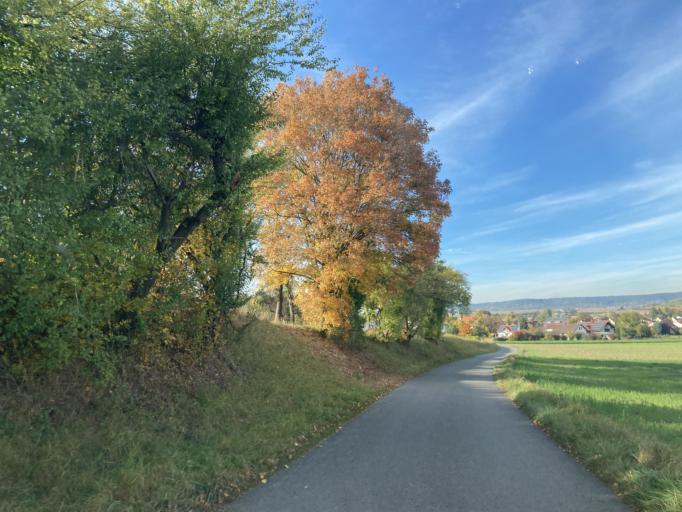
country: DE
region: Baden-Wuerttemberg
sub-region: Tuebingen Region
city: Rottenburg
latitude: 48.5211
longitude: 8.9644
